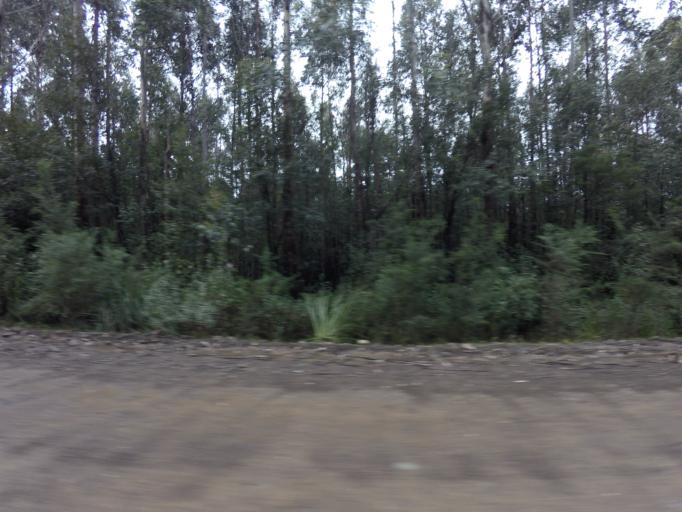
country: AU
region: Tasmania
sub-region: Huon Valley
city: Geeveston
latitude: -43.4729
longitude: 146.8920
